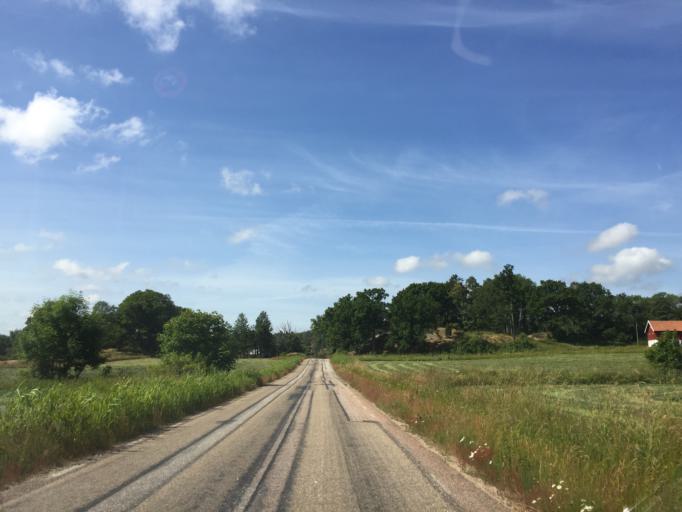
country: SE
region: Vaestra Goetaland
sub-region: Orust
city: Henan
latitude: 58.3136
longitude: 11.6828
